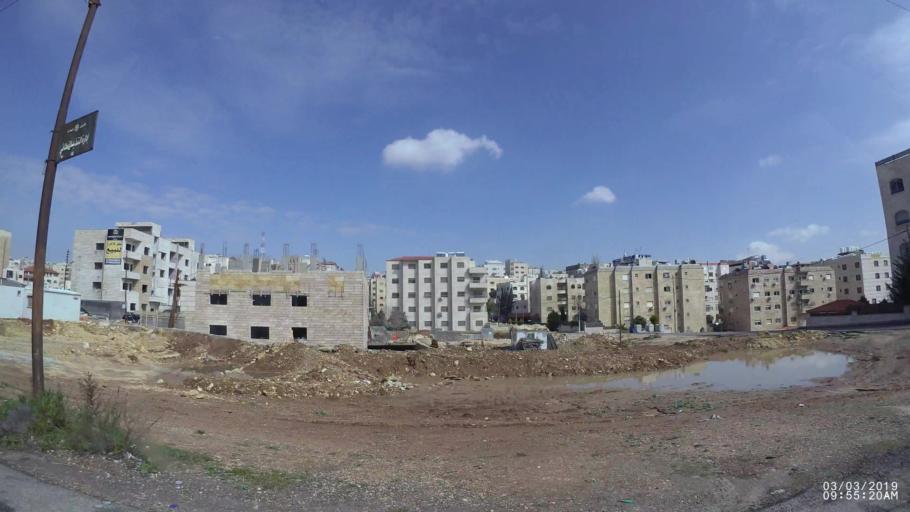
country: JO
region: Amman
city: Al Jubayhah
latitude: 31.9941
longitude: 35.8973
